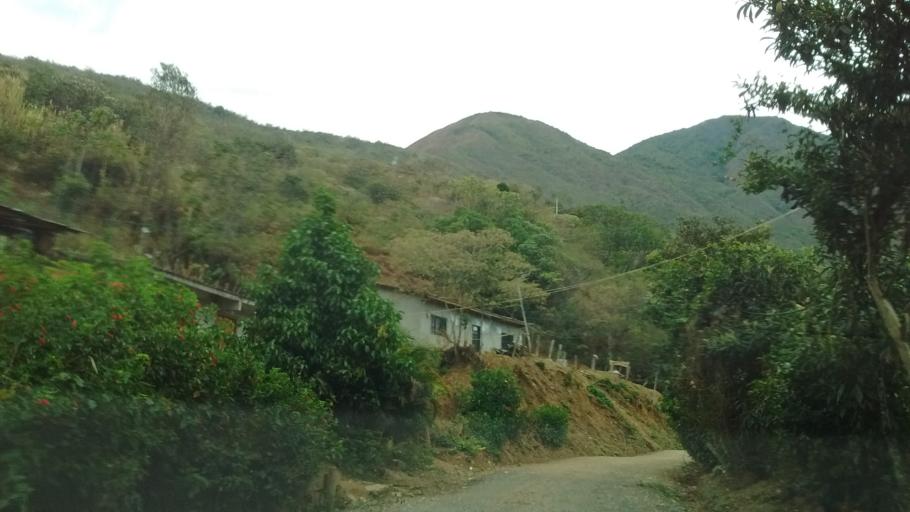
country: CO
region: Cauca
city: Almaguer
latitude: 1.8464
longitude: -76.9033
